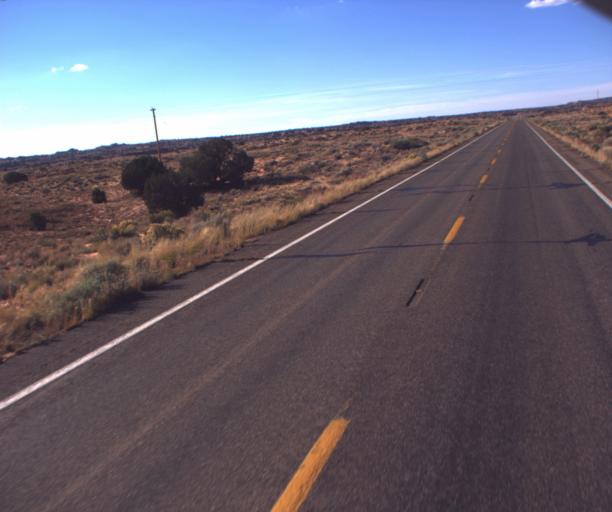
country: US
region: Arizona
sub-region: Coconino County
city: Kaibito
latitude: 36.6041
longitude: -111.1758
